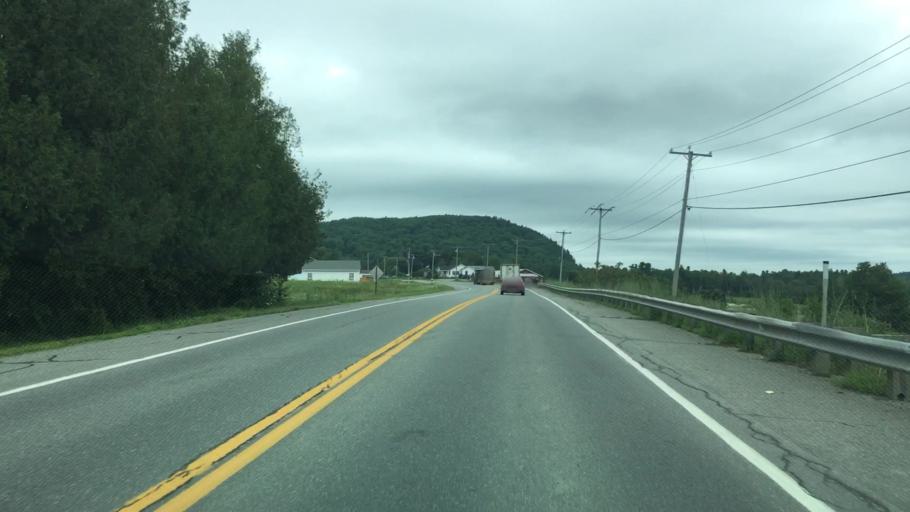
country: US
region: Maine
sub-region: Waldo County
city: Frankfort
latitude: 44.5614
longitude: -68.8663
